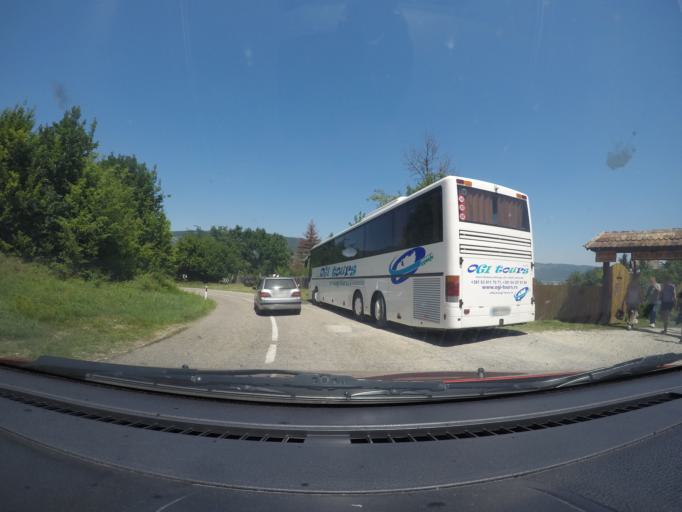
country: RO
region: Mehedinti
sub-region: Comuna Svinita
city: Svinita
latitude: 44.4726
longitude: 22.1056
